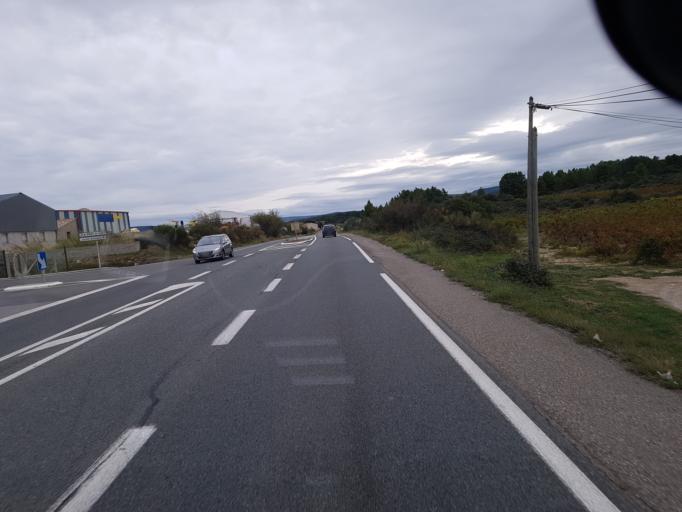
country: FR
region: Languedoc-Roussillon
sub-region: Departement de l'Aude
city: Peyriac-de-Mer
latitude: 43.1276
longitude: 2.9599
